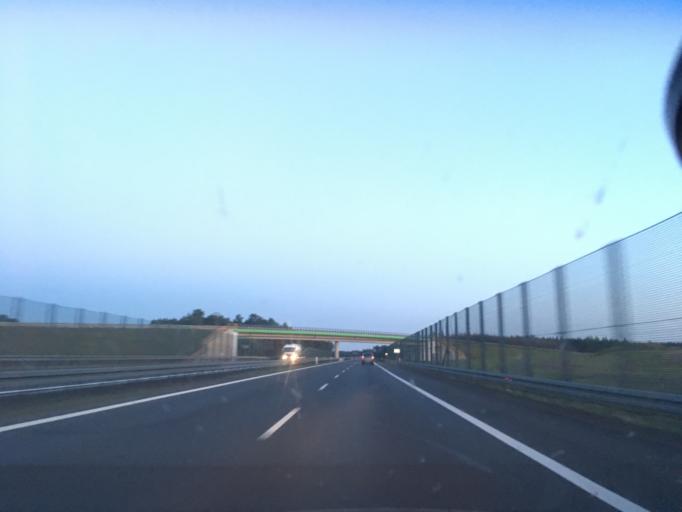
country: PL
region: Lubusz
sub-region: Powiat miedzyrzecki
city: Skwierzyna
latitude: 52.5710
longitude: 15.4710
